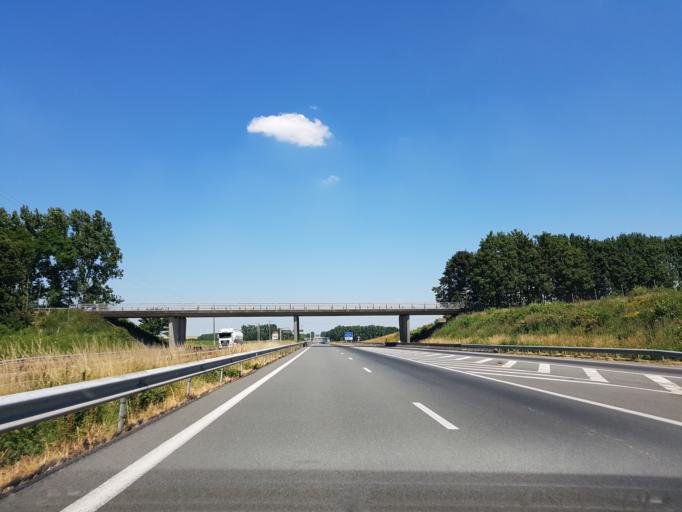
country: FR
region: Nord-Pas-de-Calais
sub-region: Departement du Nord
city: Marcoing
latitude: 50.0720
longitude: 3.1766
